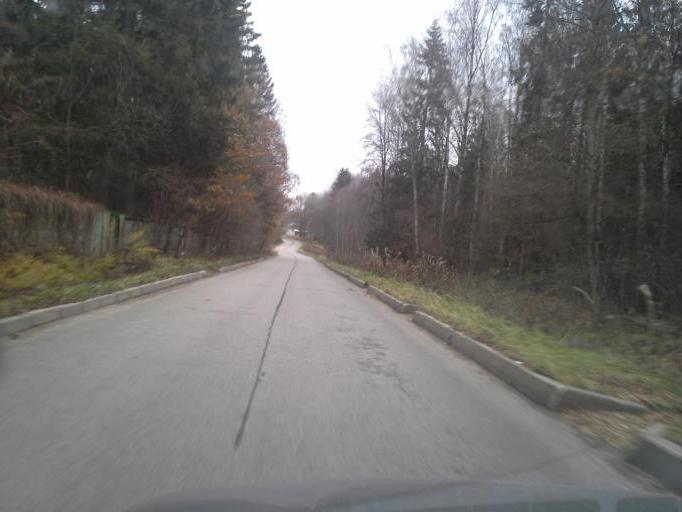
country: RU
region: Moskovskaya
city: Peshki
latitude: 56.1476
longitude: 37.0463
